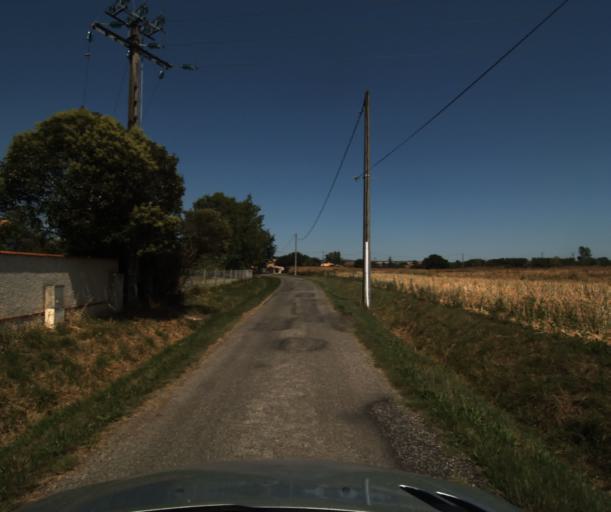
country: FR
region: Midi-Pyrenees
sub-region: Departement de la Haute-Garonne
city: Saubens
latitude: 43.4735
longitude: 1.3611
